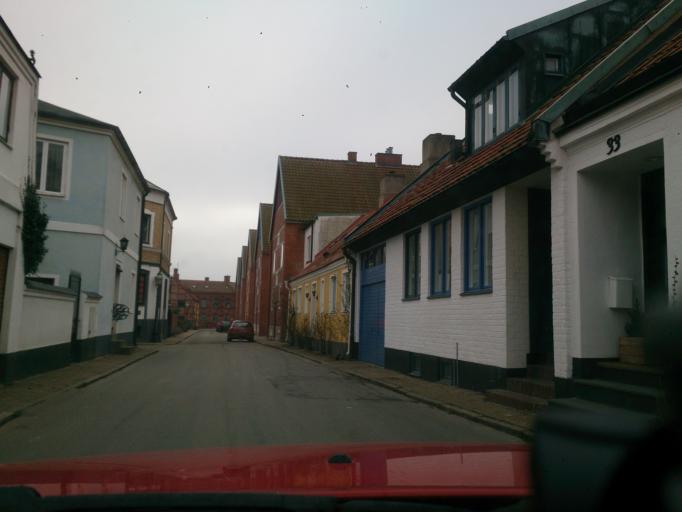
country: SE
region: Skane
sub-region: Ystads Kommun
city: Ystad
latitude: 55.4306
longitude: 13.8154
